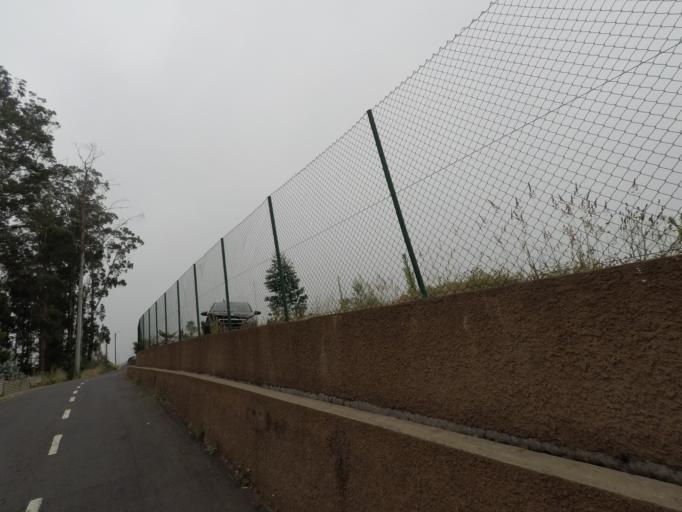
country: PT
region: Madeira
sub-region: Camara de Lobos
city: Curral das Freiras
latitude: 32.6876
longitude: -16.9478
